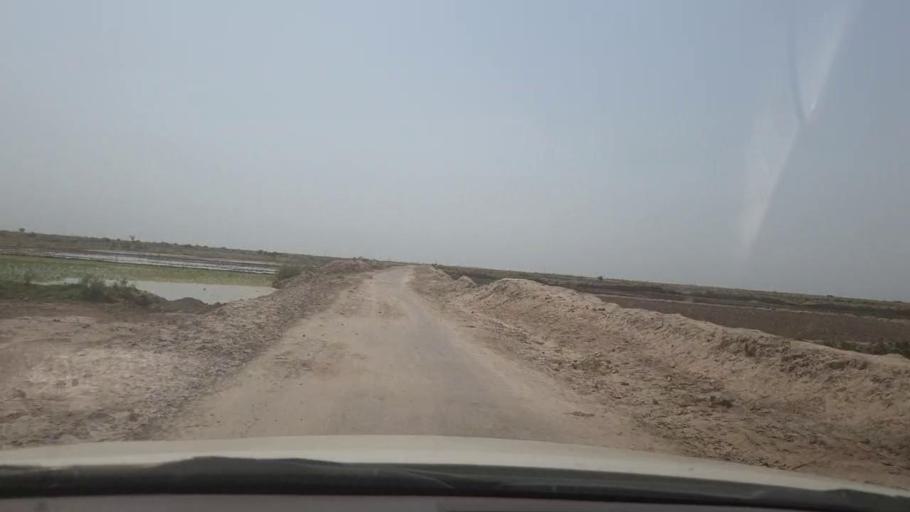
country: PK
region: Sindh
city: Garhi Yasin
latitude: 27.9889
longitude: 68.5126
